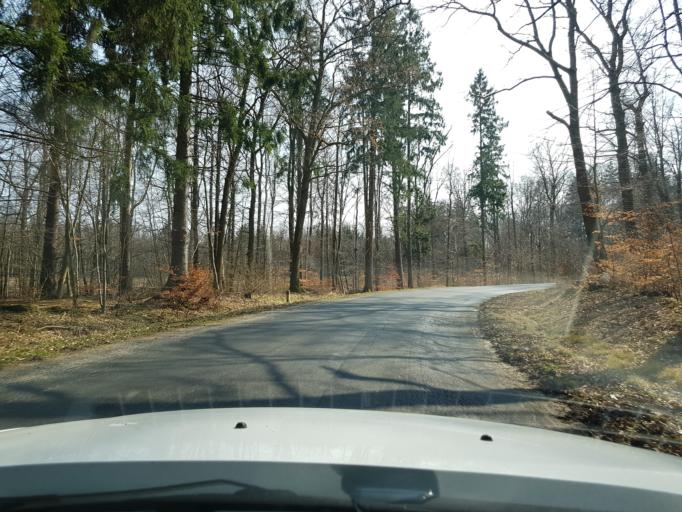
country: PL
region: West Pomeranian Voivodeship
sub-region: Powiat koszalinski
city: Sianow
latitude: 54.2608
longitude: 16.3142
